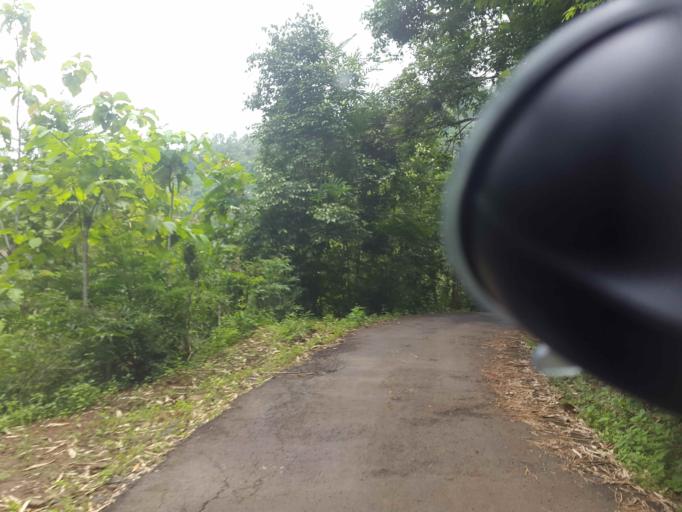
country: ID
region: Central Java
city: Binangun
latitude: -7.5259
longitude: 109.2418
